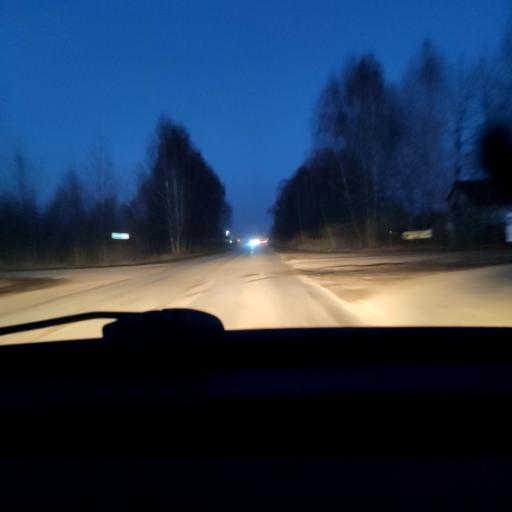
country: RU
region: Bashkortostan
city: Ufa
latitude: 54.6669
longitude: 56.0779
